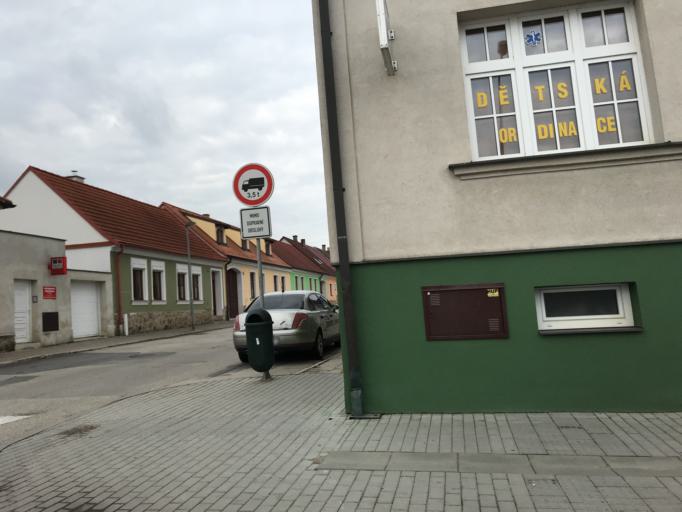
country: CZ
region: Jihocesky
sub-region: Okres Jindrichuv Hradec
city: Trebon
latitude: 49.0072
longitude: 14.7577
